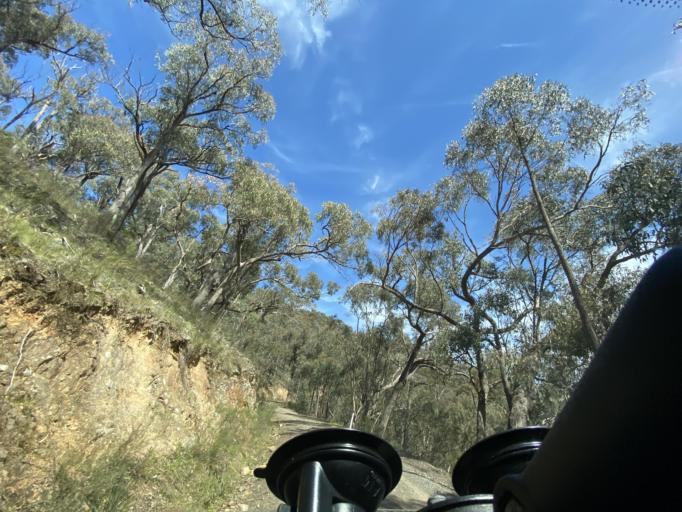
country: AU
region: Victoria
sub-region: Mansfield
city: Mansfield
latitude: -36.8089
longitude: 146.1028
